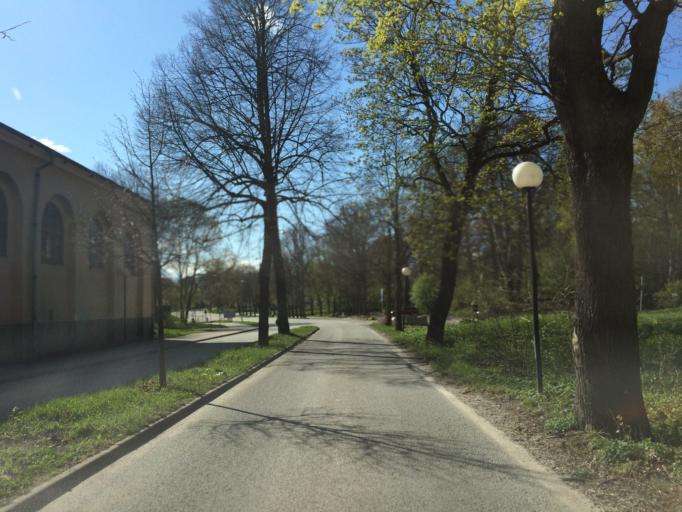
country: SE
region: Stockholm
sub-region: Norrtalje Kommun
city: Bergshamra
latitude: 59.3696
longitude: 18.0272
